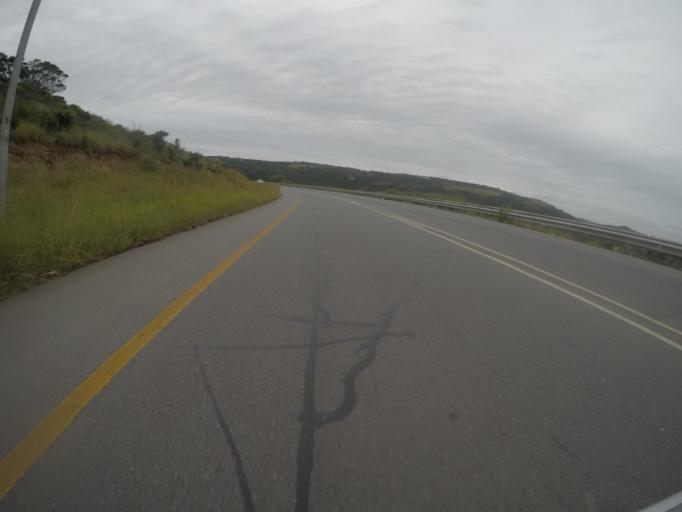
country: ZA
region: Eastern Cape
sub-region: Buffalo City Metropolitan Municipality
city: East London
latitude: -32.9540
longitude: 27.9140
